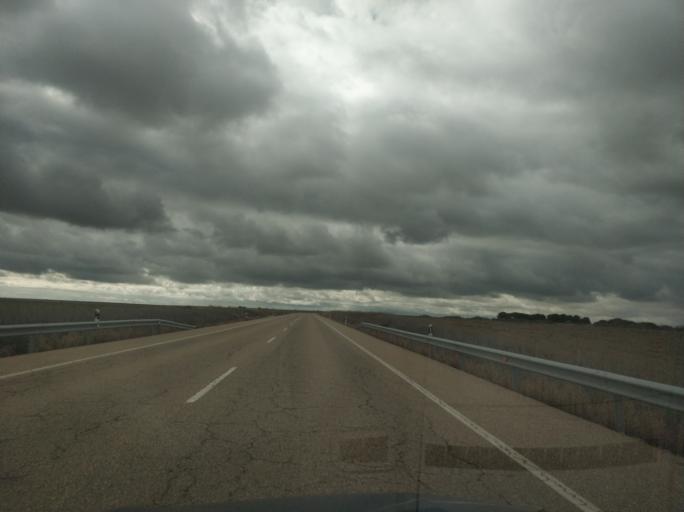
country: ES
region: Castille and Leon
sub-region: Provincia de Valladolid
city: Alaejos
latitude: 41.2723
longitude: -5.2559
